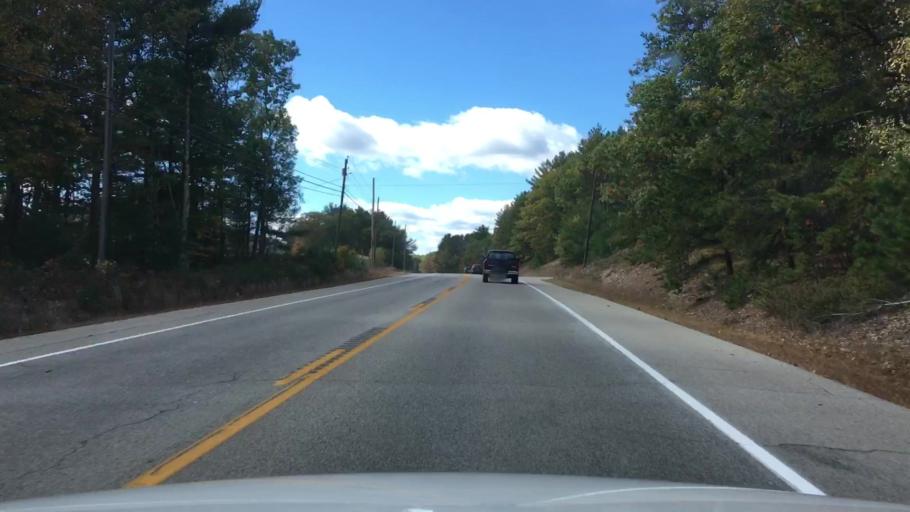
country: US
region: Maine
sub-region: York County
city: Alfred
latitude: 43.4790
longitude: -70.6353
